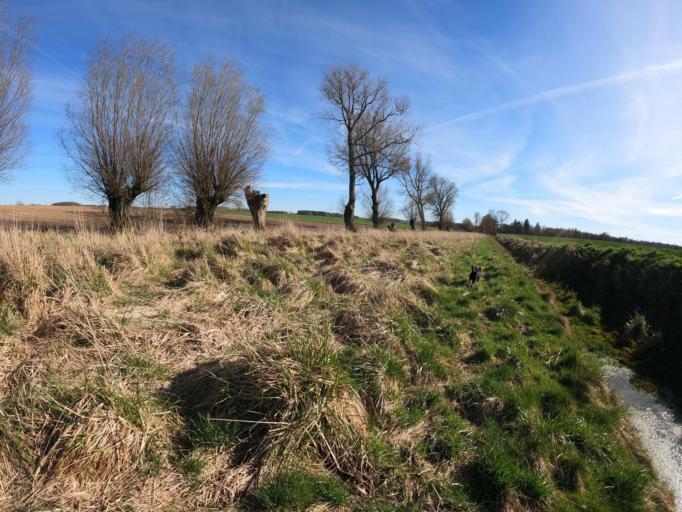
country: PL
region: West Pomeranian Voivodeship
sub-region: Powiat gryficki
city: Brojce
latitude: 53.9173
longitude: 15.3238
